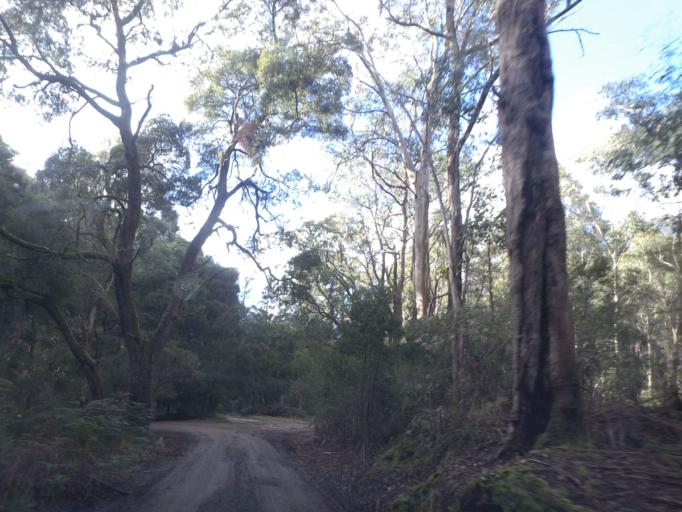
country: AU
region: Victoria
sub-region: Moorabool
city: Bacchus Marsh
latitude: -37.4647
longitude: 144.3068
